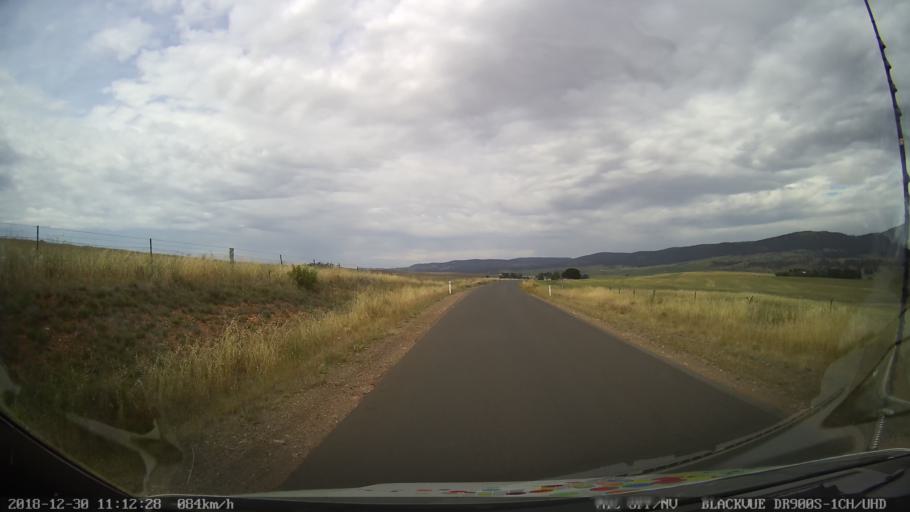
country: AU
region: New South Wales
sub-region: Snowy River
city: Jindabyne
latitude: -36.5286
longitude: 148.7565
